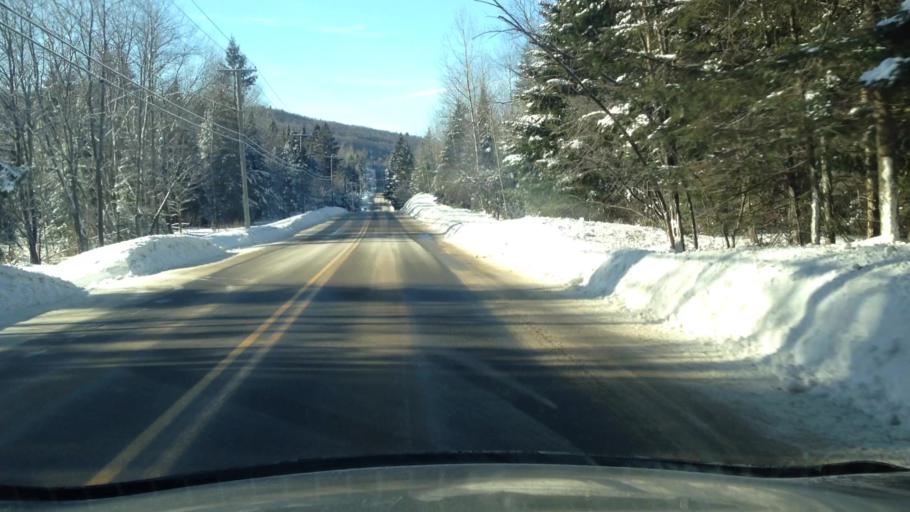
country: CA
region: Quebec
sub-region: Laurentides
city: Sainte-Agathe-des-Monts
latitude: 45.9303
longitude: -74.4169
